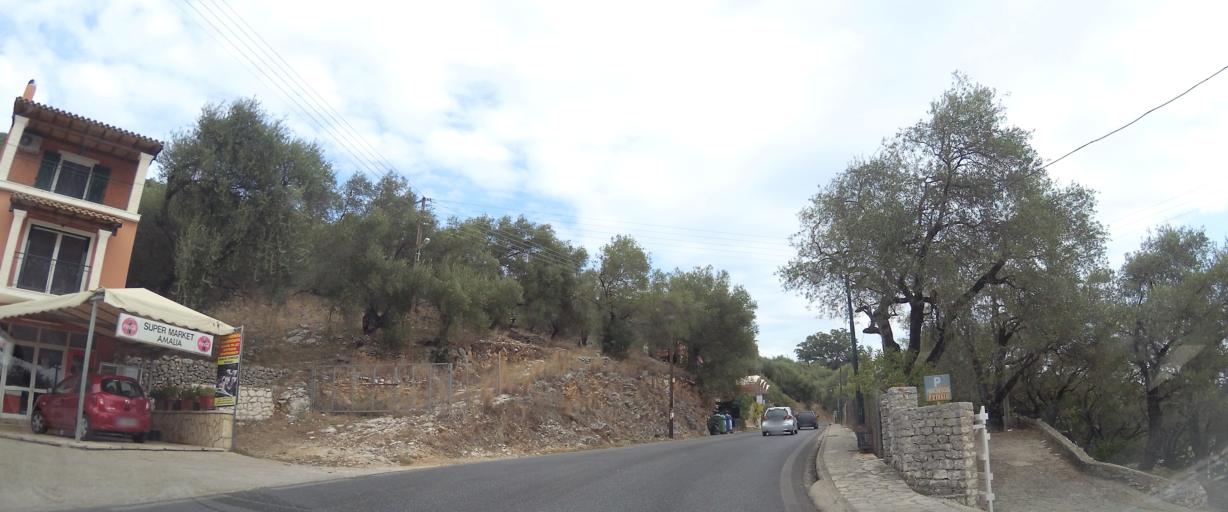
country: GR
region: Ionian Islands
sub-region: Nomos Kerkyras
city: Kontokali
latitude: 39.7271
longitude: 19.8980
